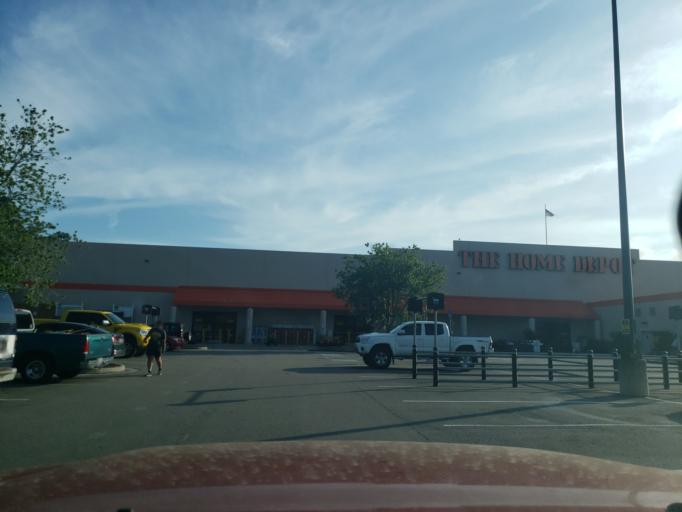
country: US
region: Georgia
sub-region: Chatham County
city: Montgomery
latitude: 31.9823
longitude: -81.1447
